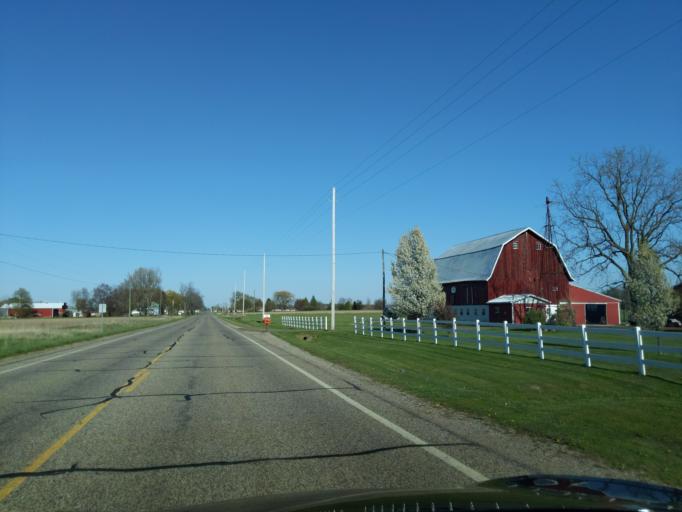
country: US
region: Michigan
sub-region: Ionia County
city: Ionia
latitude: 42.8859
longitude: -85.0400
